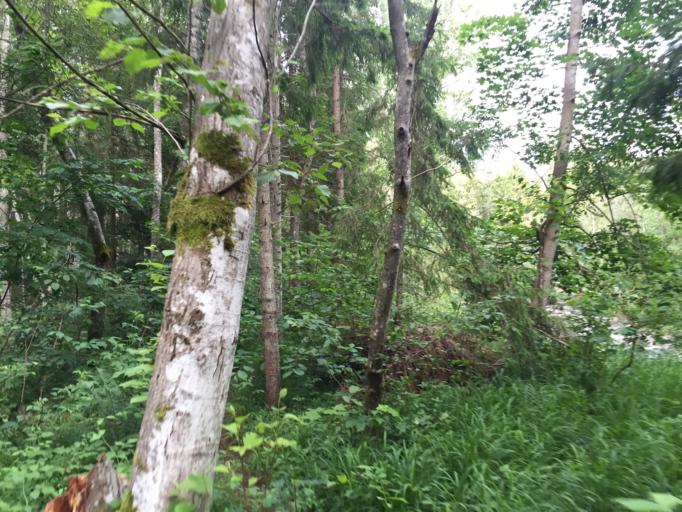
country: LV
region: Ligatne
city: Ligatne
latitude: 57.2330
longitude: 25.1512
